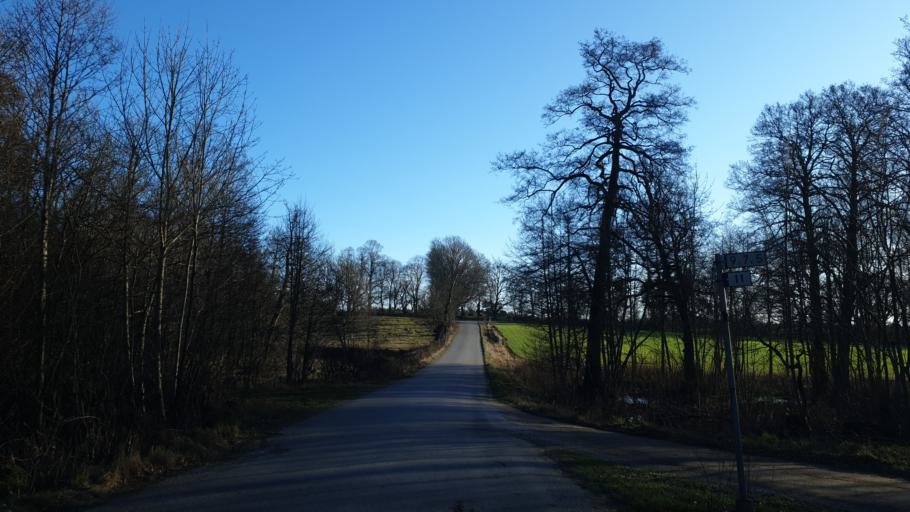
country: SE
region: Blekinge
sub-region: Karlskrona Kommun
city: Nattraby
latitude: 56.2454
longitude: 15.4192
